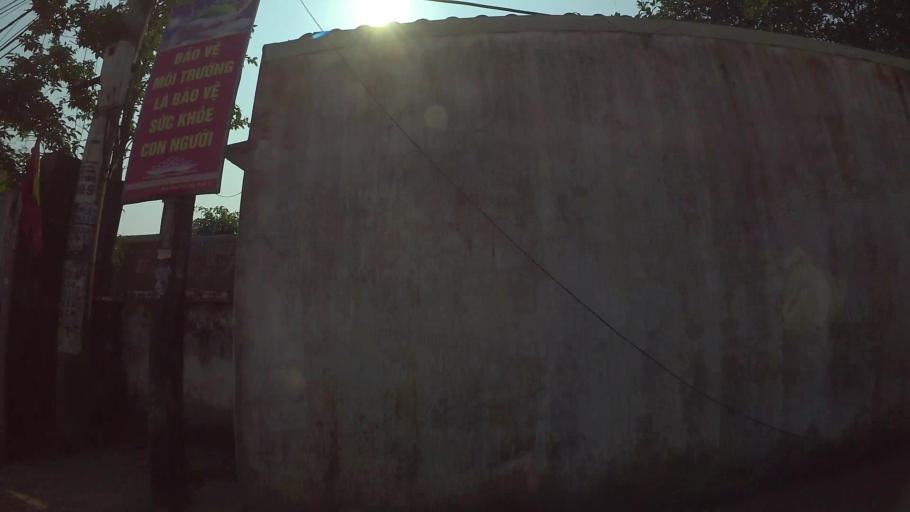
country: VN
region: Da Nang
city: Cam Le
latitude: 16.0139
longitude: 108.1865
